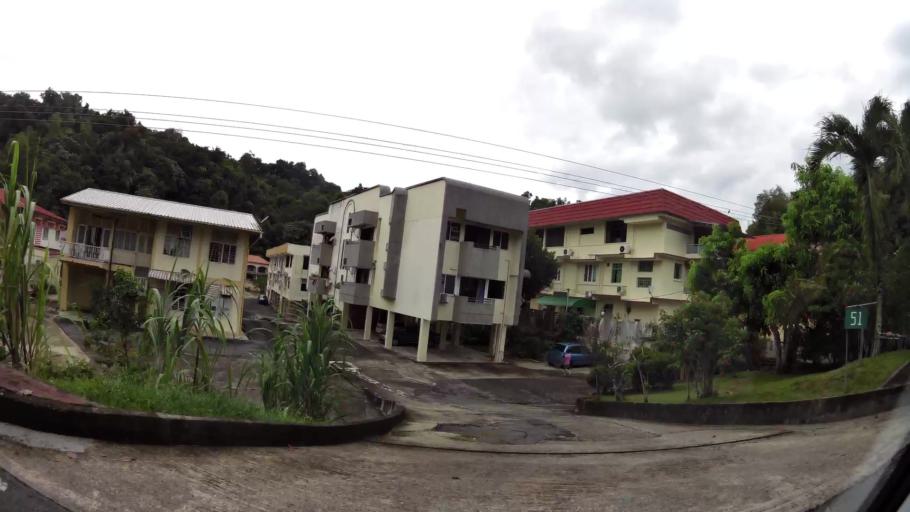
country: BN
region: Brunei and Muara
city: Bandar Seri Begawan
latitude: 4.8950
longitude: 114.9479
